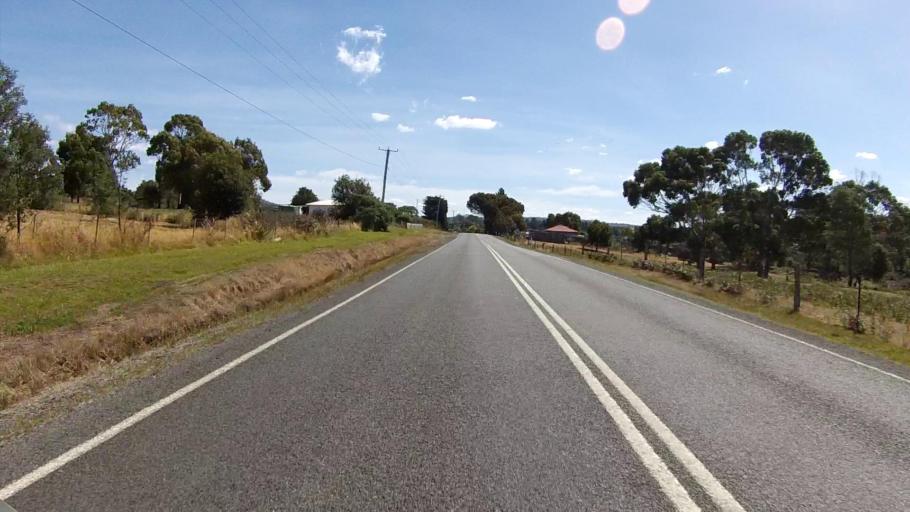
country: AU
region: Tasmania
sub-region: Sorell
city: Sorell
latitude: -42.6109
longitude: 147.7322
